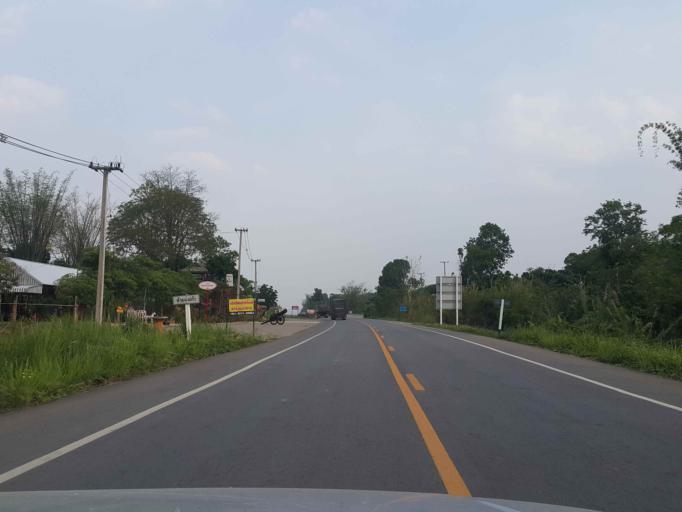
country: TH
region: Chiang Mai
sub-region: Amphoe Chiang Dao
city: Chiang Dao
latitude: 19.3691
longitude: 98.9490
